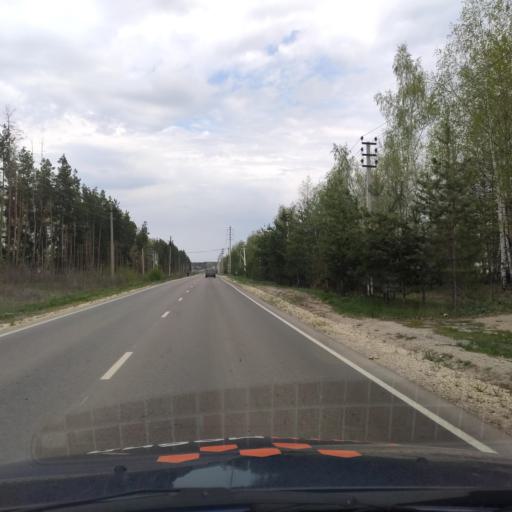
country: RU
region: Voronezj
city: Podgornoye
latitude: 51.8611
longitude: 39.1659
